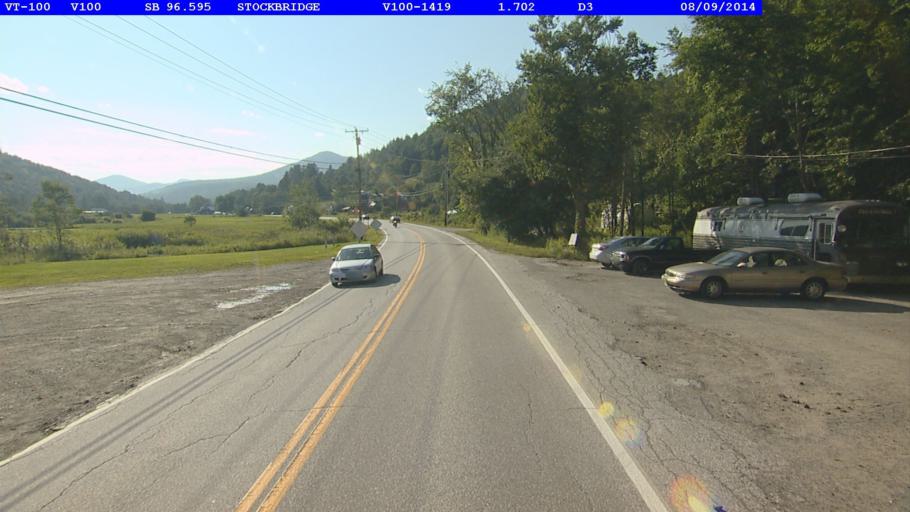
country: US
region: Vermont
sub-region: Orange County
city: Randolph
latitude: 43.7759
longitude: -72.7658
